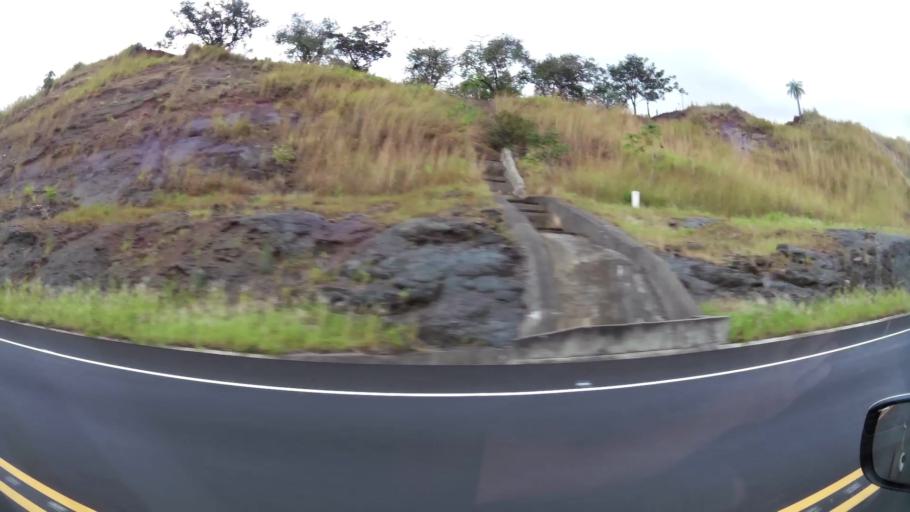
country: CR
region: Alajuela
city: Atenas
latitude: 9.9357
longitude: -84.4207
